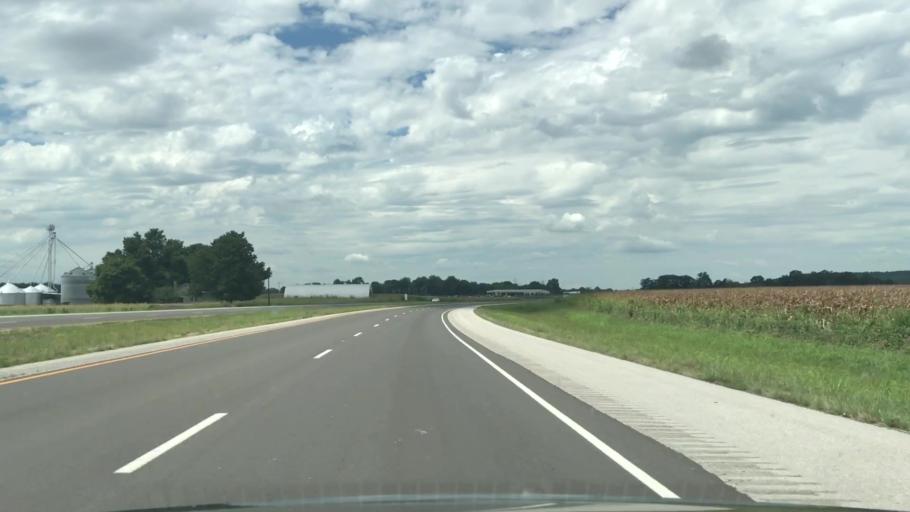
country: US
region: Kentucky
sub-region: Todd County
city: Elkton
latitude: 36.8065
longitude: -87.0520
